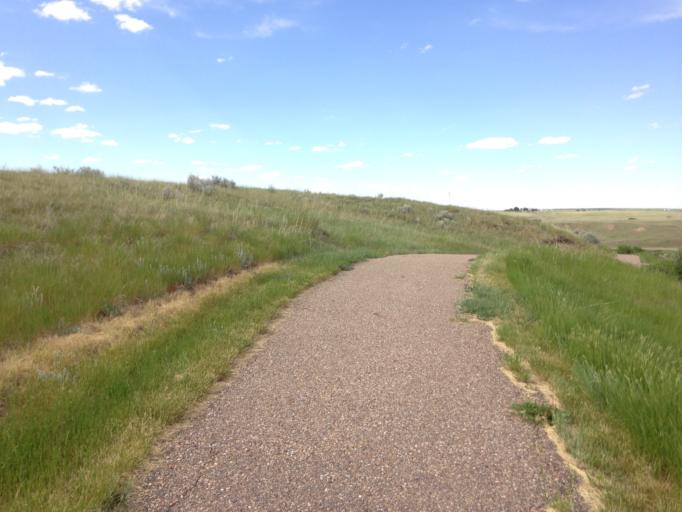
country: CA
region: Alberta
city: Medicine Hat
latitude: 50.0132
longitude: -110.6227
